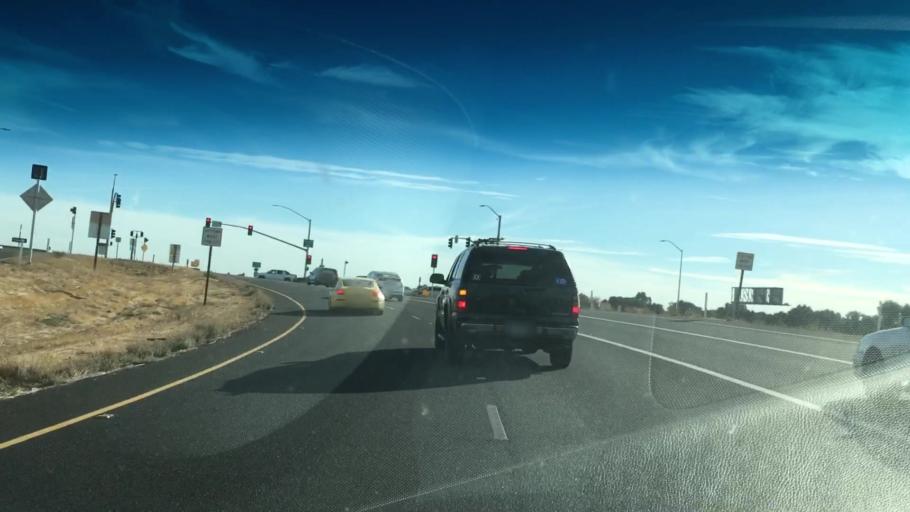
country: US
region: California
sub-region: Sacramento County
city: Parkway
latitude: 38.4670
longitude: -121.4998
